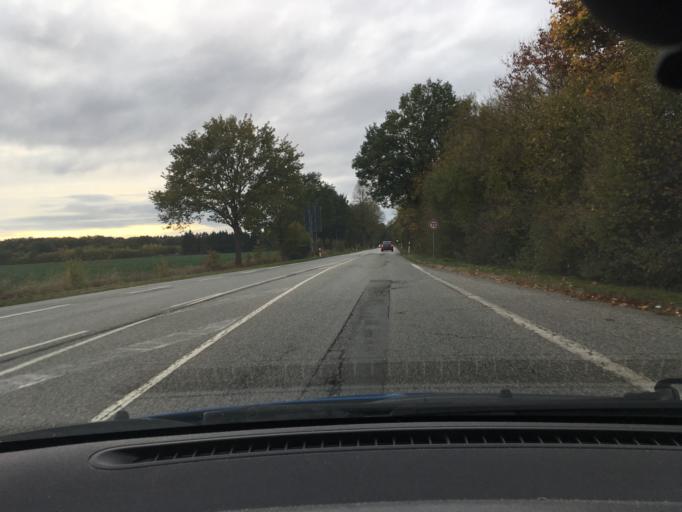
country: DE
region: Schleswig-Holstein
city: Hohenhorn
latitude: 53.4892
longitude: 10.3618
